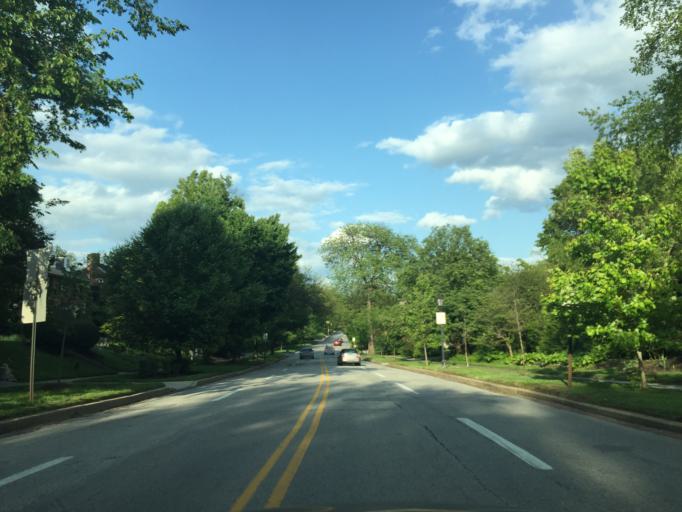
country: US
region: Maryland
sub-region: City of Baltimore
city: Baltimore
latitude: 39.3362
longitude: -76.6120
